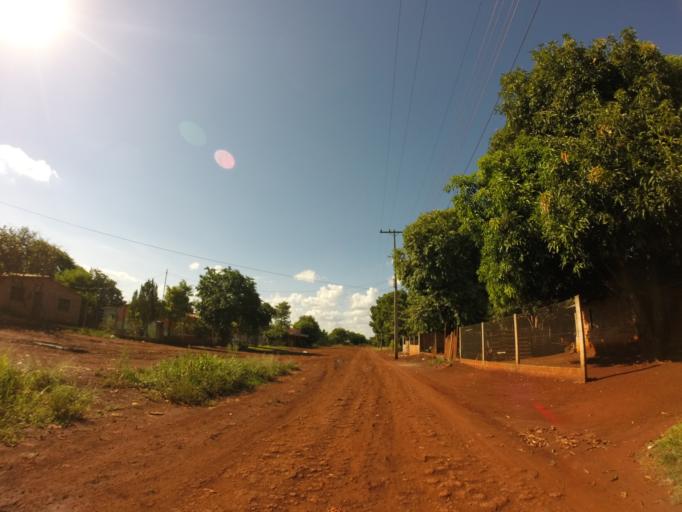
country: PY
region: Alto Parana
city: Ciudad del Este
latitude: -25.3706
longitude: -54.6475
